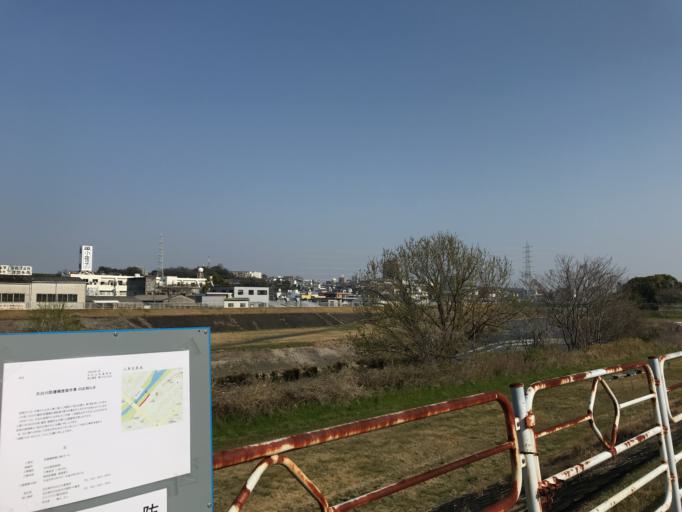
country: JP
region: Aichi
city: Nagoya-shi
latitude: 35.1228
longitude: 136.9742
